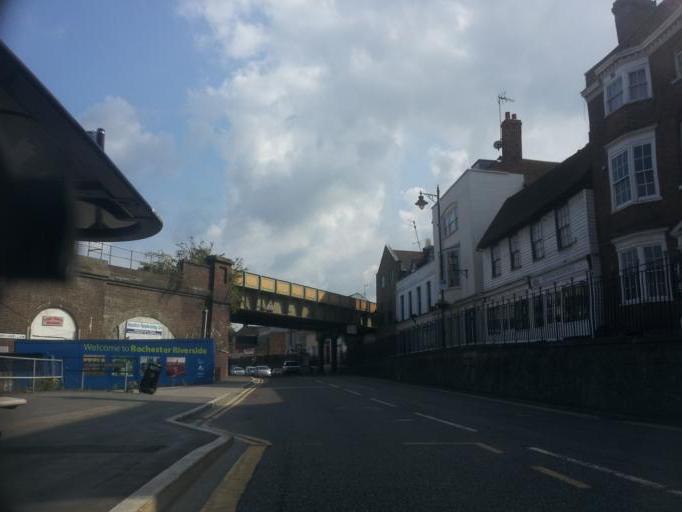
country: GB
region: England
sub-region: Medway
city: Rochester
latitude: 51.3841
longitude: 0.5115
